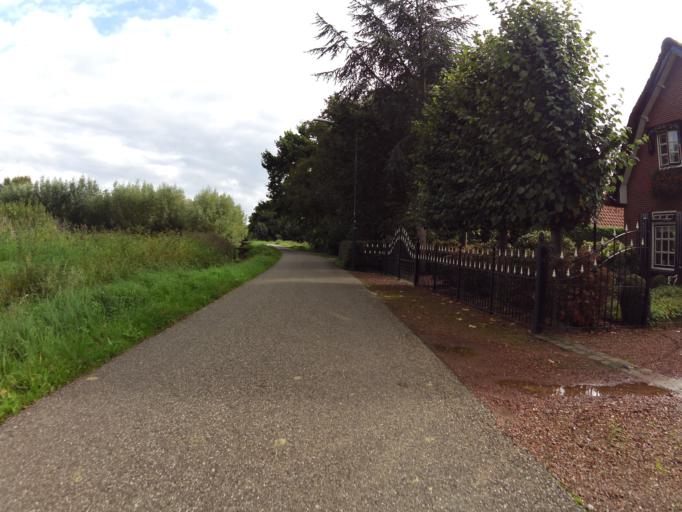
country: NL
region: North Holland
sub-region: Gemeente Wijdemeren
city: Oud-Loosdrecht
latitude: 52.1743
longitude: 5.0937
